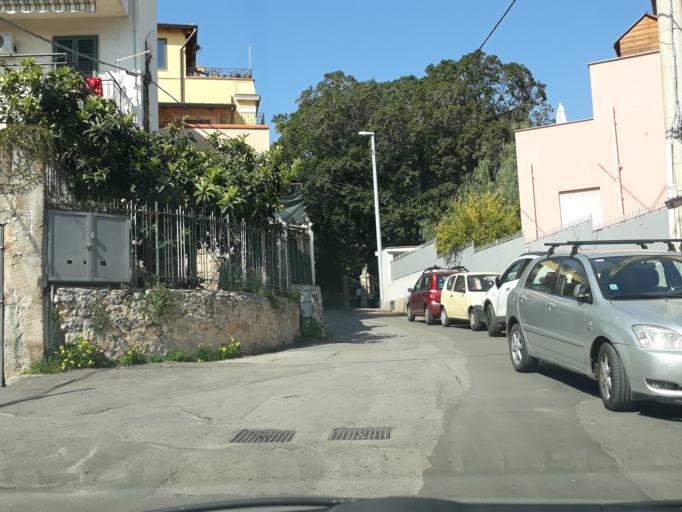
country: IT
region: Sicily
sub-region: Palermo
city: Piano dei Geli
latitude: 38.1091
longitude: 13.3044
